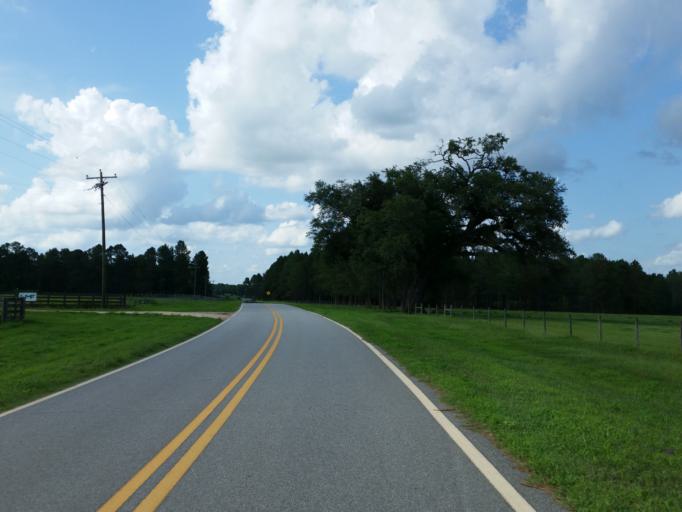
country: US
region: Georgia
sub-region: Lee County
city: Leesburg
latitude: 31.7498
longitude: -84.0393
